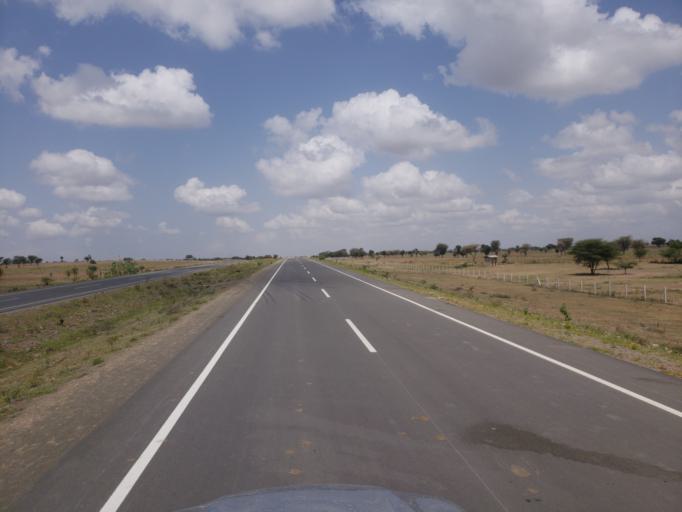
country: ET
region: Oromiya
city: Mojo
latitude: 8.3222
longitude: 38.9557
